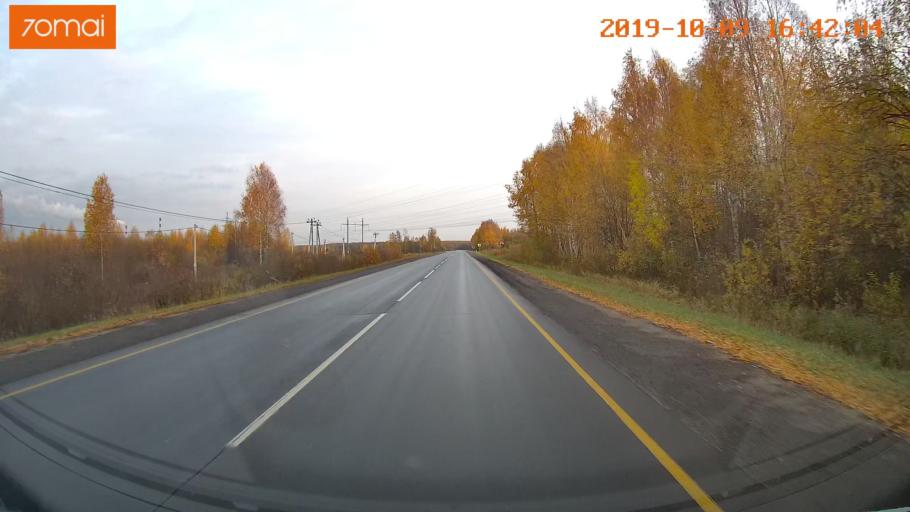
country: RU
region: Kostroma
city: Volgorechensk
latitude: 57.4662
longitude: 41.0932
